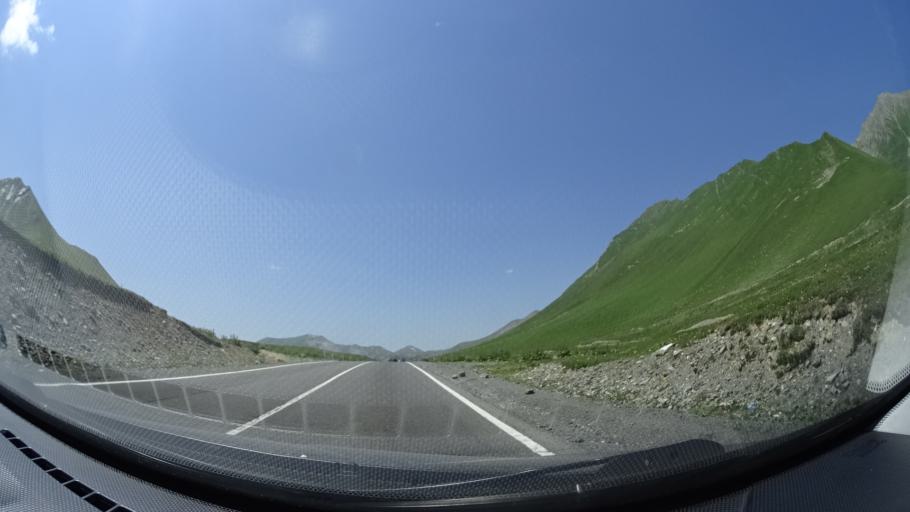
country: GE
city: Gudauri
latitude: 42.5171
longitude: 44.4655
